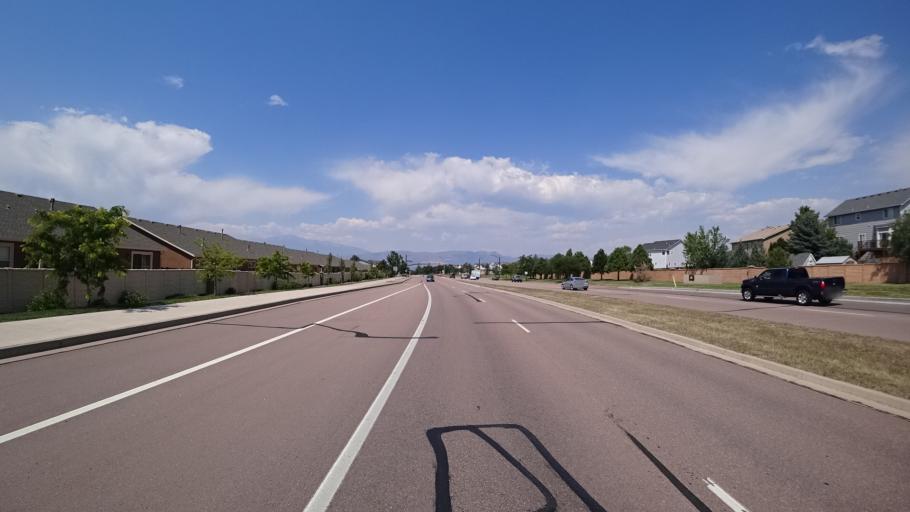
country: US
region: Colorado
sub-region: El Paso County
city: Cimarron Hills
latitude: 38.9294
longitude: -104.7262
